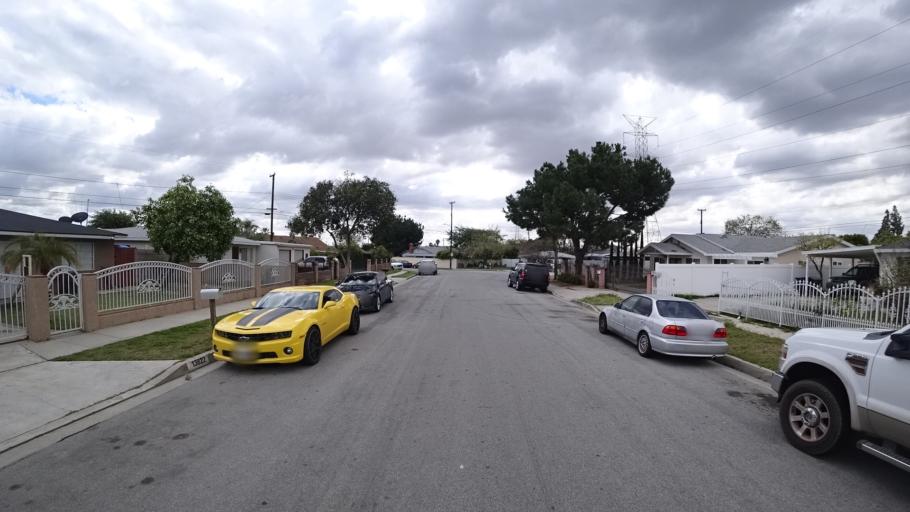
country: US
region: California
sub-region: Los Angeles County
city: Baldwin Park
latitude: 34.1034
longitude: -117.9720
